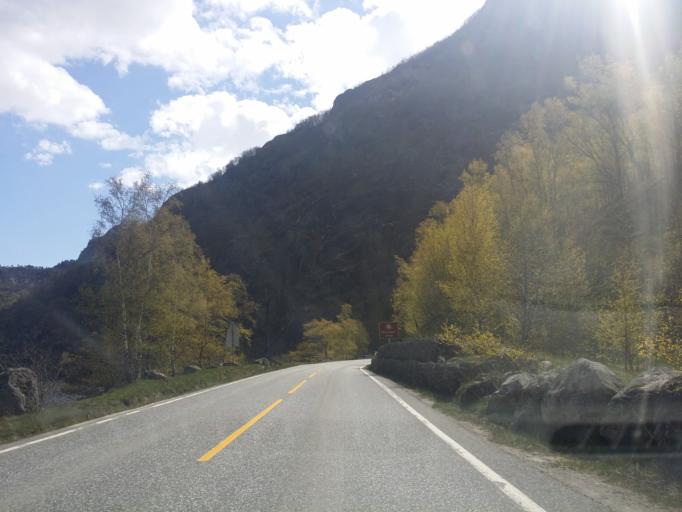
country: NO
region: Hordaland
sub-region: Eidfjord
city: Eidfjord
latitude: 60.4554
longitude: 7.0925
